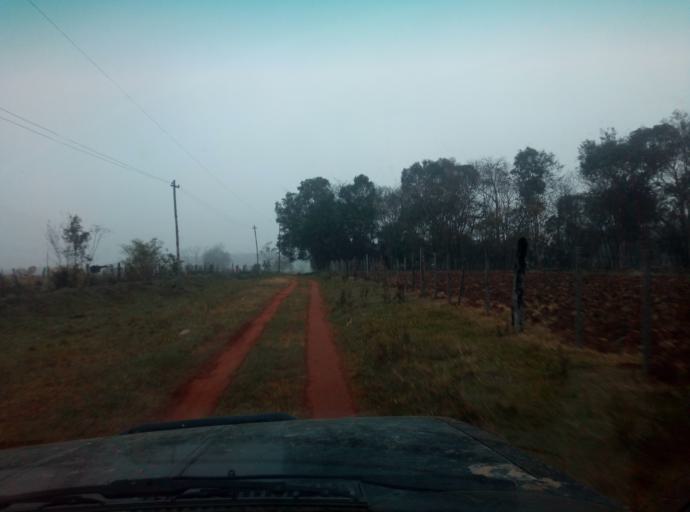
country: PY
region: Caaguazu
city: Doctor Cecilio Baez
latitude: -25.1578
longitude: -56.2615
